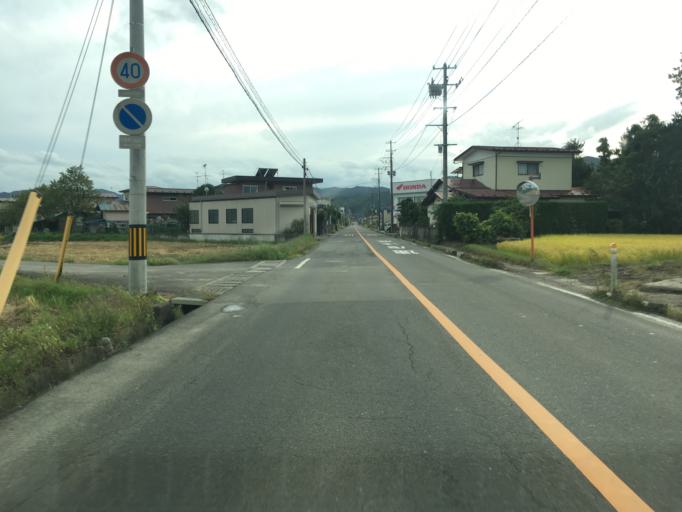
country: JP
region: Miyagi
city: Marumori
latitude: 37.9277
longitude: 140.7725
